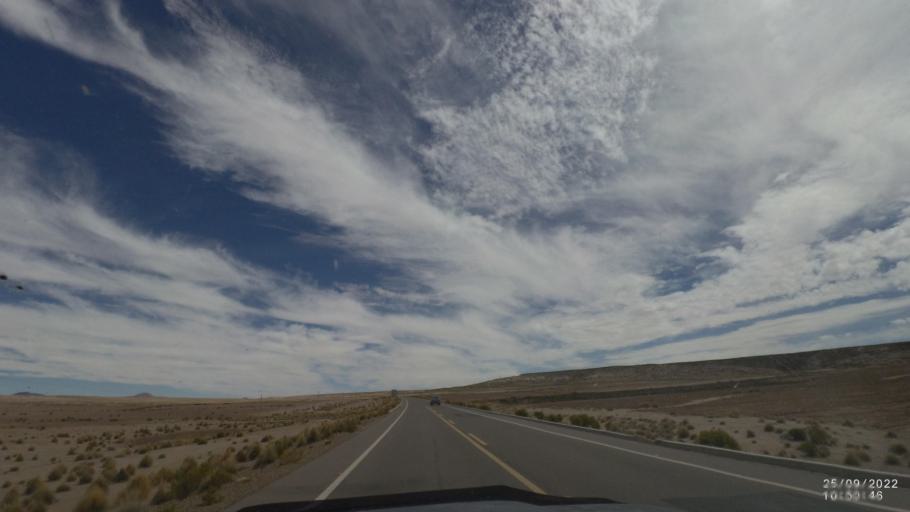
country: BO
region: Oruro
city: Challapata
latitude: -19.5710
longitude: -66.8410
